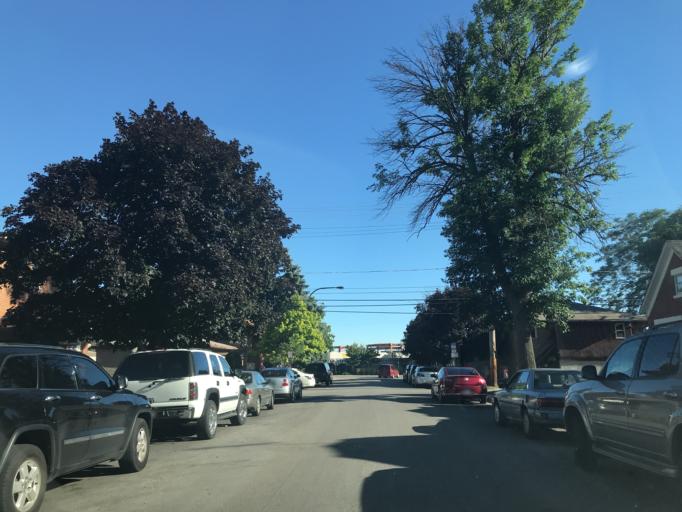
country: US
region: Illinois
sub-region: Cook County
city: Cicero
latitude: 41.8445
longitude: -87.7663
